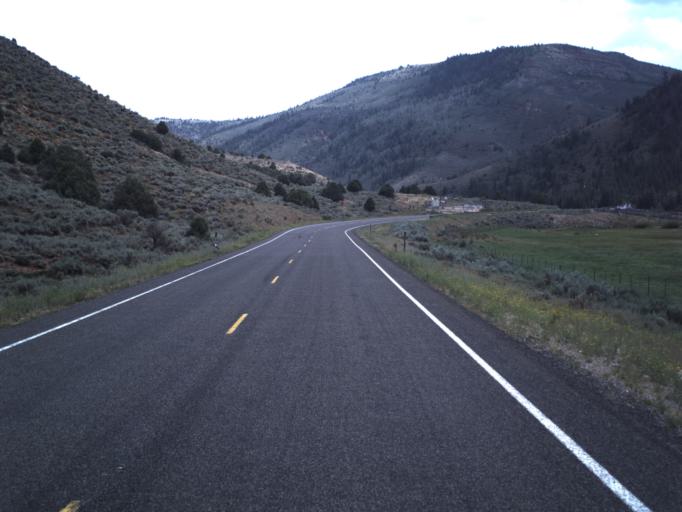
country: US
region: Utah
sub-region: Summit County
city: Francis
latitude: 40.4530
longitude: -110.8740
